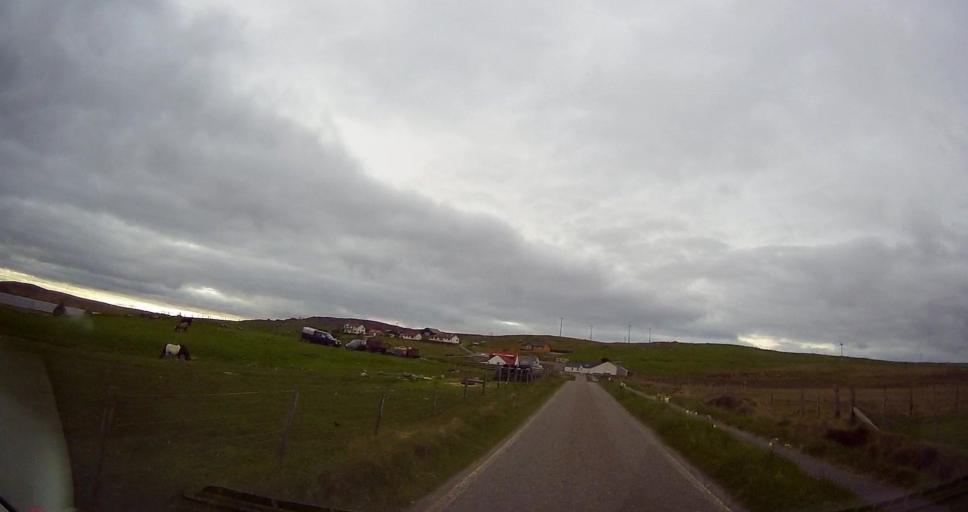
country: GB
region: Scotland
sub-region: Shetland Islands
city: Shetland
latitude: 60.5002
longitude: -1.0592
